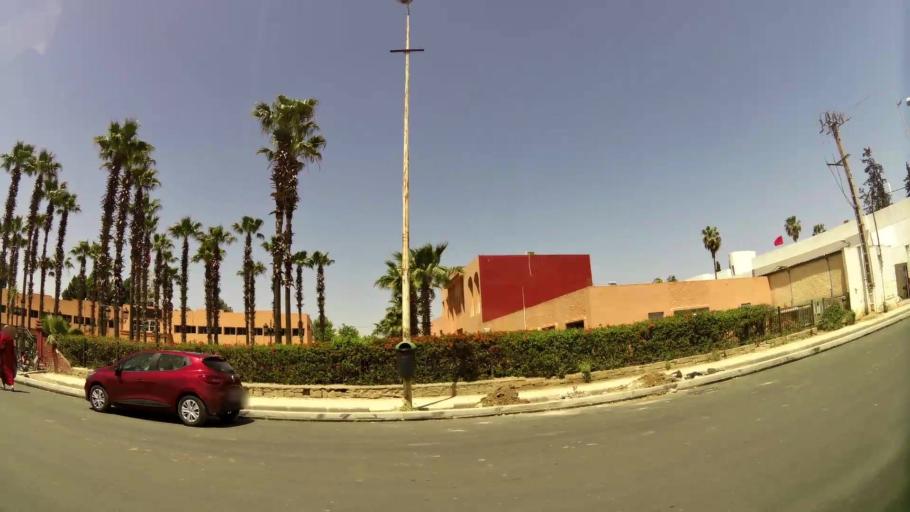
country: MA
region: Rabat-Sale-Zemmour-Zaer
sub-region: Khemisset
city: Khemisset
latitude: 33.8244
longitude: -6.0715
